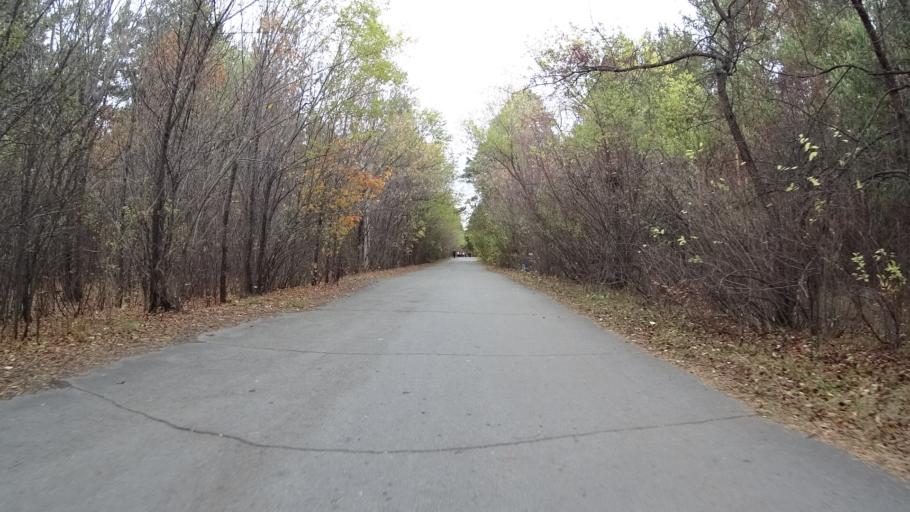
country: RU
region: Chelyabinsk
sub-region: Gorod Chelyabinsk
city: Chelyabinsk
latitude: 55.1500
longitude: 61.3564
